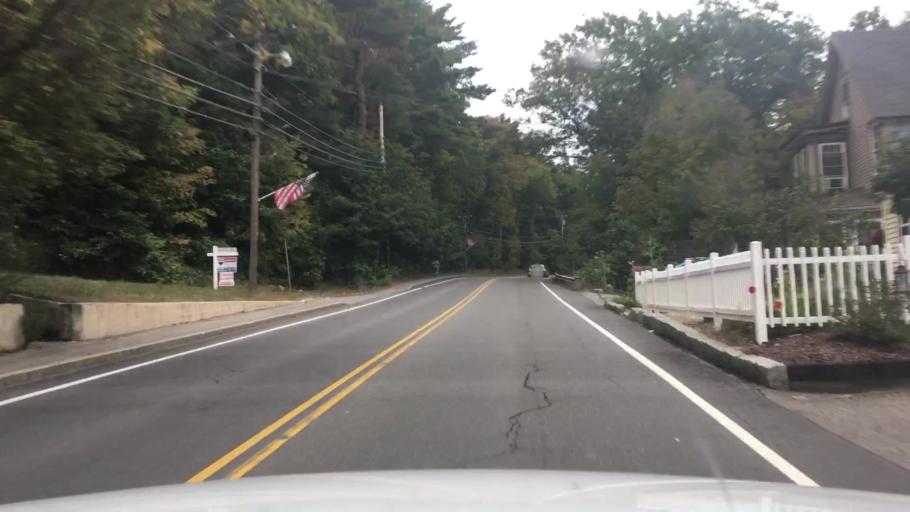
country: US
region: New Hampshire
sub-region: Strafford County
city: New Durham
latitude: 43.4636
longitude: -71.2283
